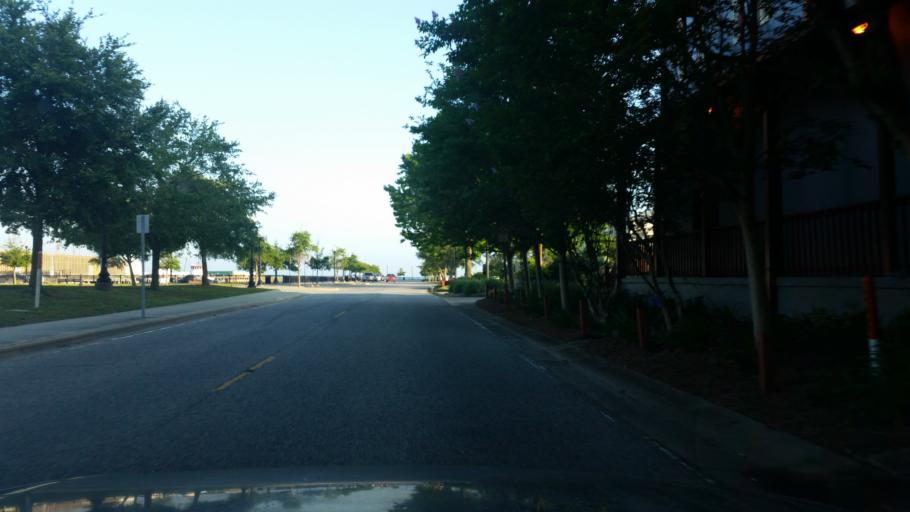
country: US
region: Florida
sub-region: Escambia County
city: Pensacola
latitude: 30.4058
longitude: -87.2128
